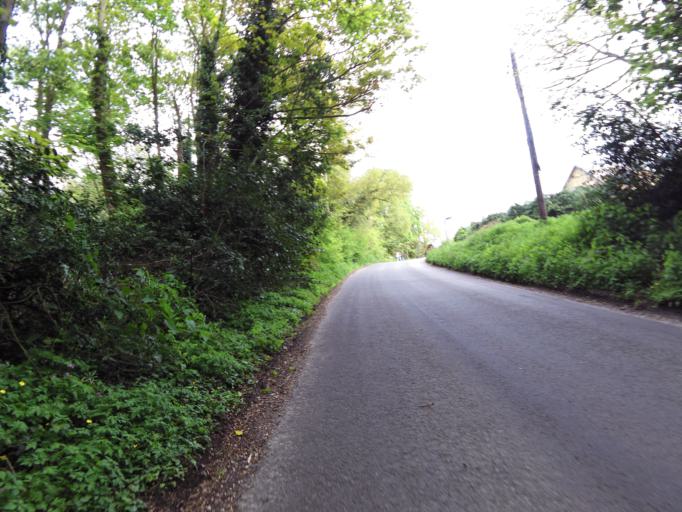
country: GB
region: England
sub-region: Suffolk
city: Ipswich
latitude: 51.9799
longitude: 1.1654
